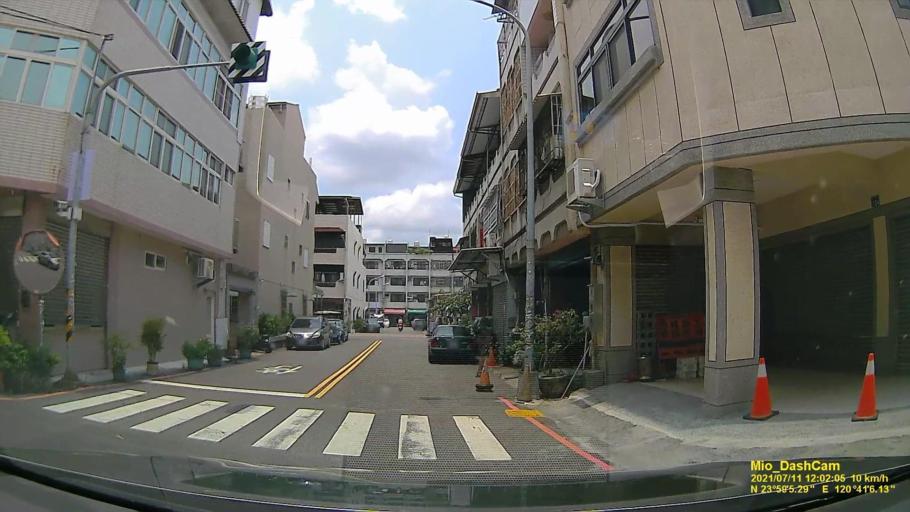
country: TW
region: Taiwan
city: Zhongxing New Village
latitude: 23.9848
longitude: 120.6850
